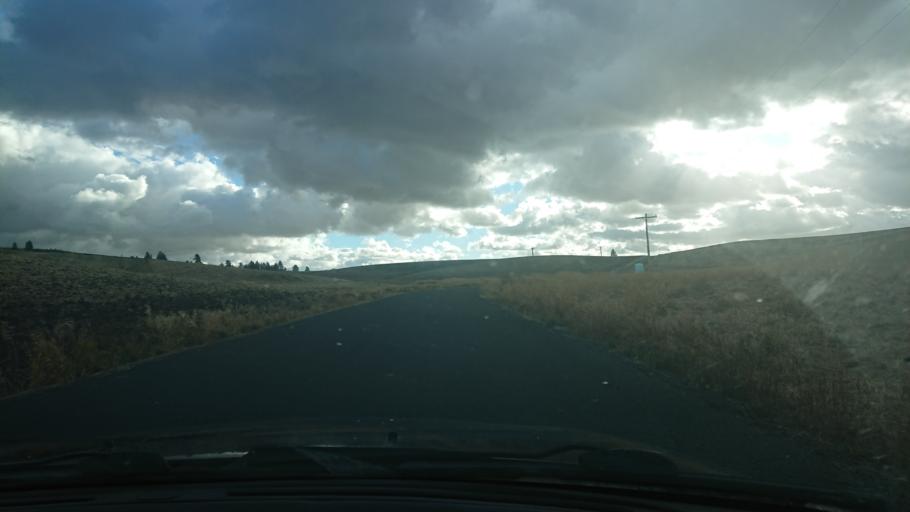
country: US
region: Idaho
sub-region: Latah County
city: Moscow
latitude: 46.6969
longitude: -116.8647
